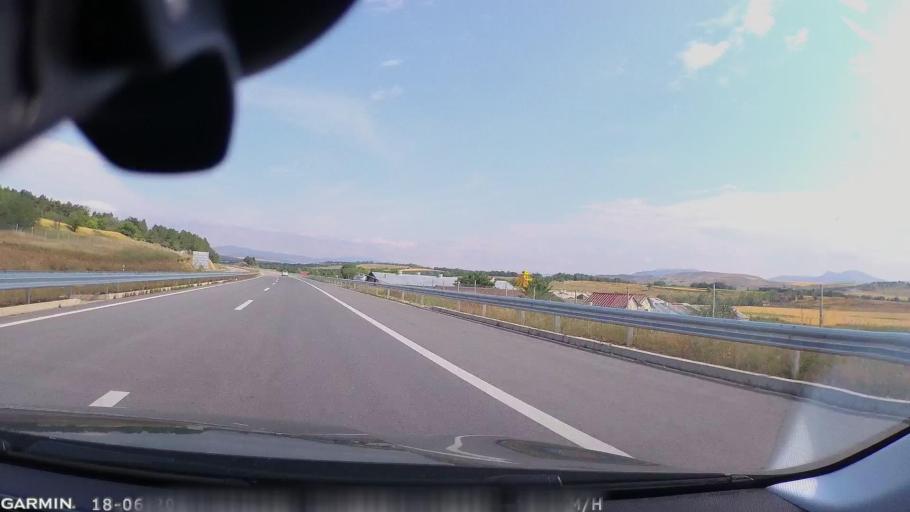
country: MK
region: Sveti Nikole
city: Sveti Nikole
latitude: 41.8835
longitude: 21.9348
